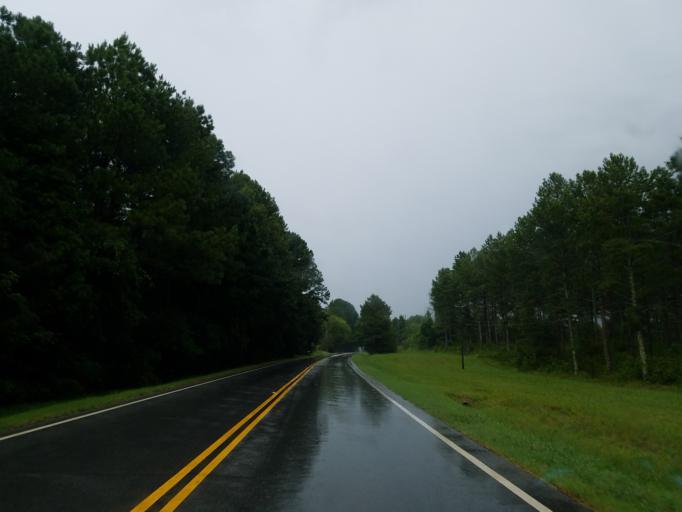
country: US
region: Georgia
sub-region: Floyd County
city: Shannon
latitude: 34.3694
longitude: -85.0851
